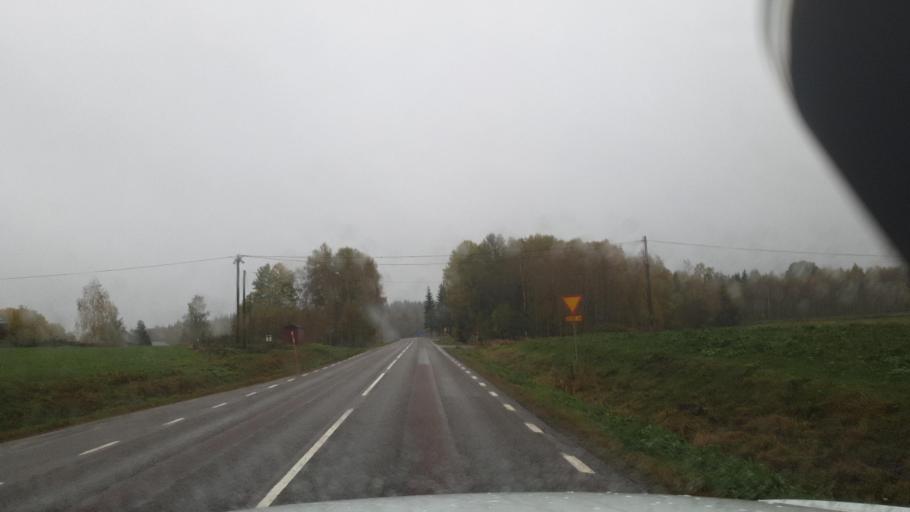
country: SE
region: Vaermland
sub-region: Eda Kommun
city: Amotfors
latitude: 59.6806
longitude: 12.3872
